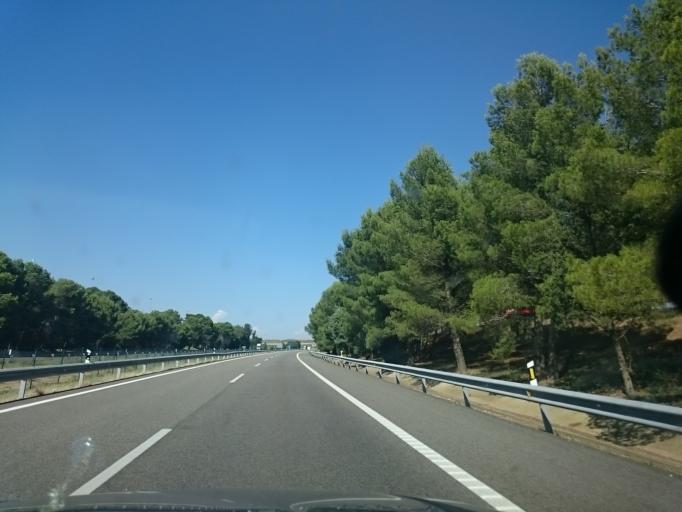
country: ES
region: Aragon
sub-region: Provincia de Huesca
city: Candasnos
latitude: 41.5177
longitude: 0.0404
